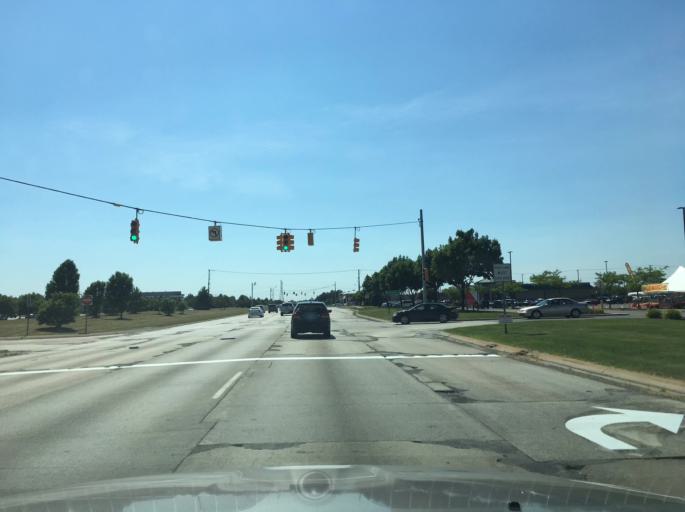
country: US
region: Michigan
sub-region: Macomb County
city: Utica
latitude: 42.6275
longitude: -82.9902
